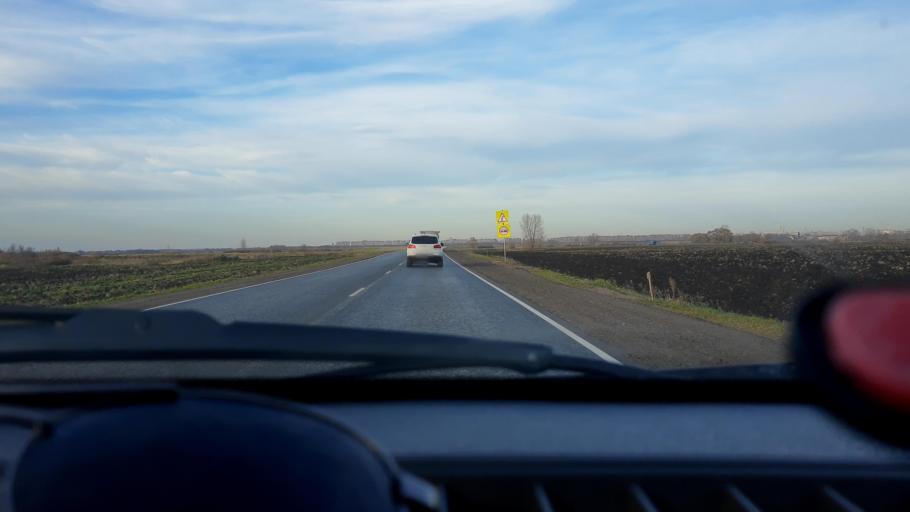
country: RU
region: Bashkortostan
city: Ufa
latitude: 54.8059
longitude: 55.9646
